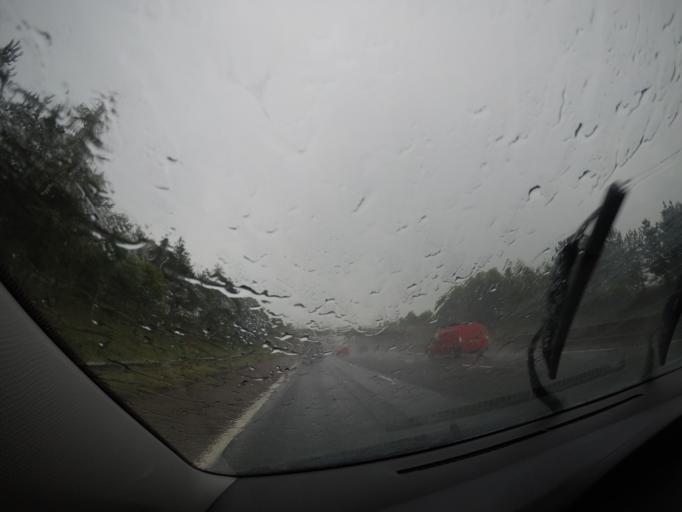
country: GB
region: England
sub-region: Cumbria
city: Penrith
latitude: 54.6920
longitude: -2.7919
